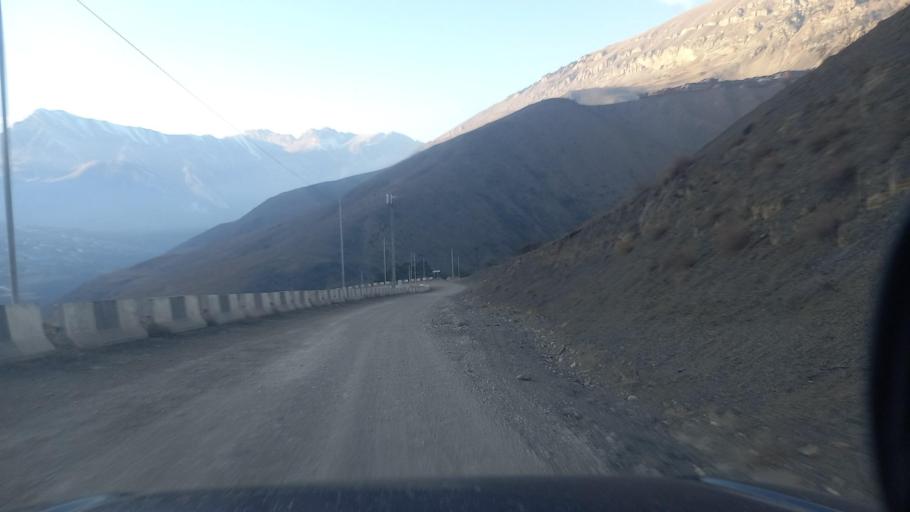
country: RU
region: Ingushetiya
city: Dzhayrakh
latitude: 42.8192
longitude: 44.7043
